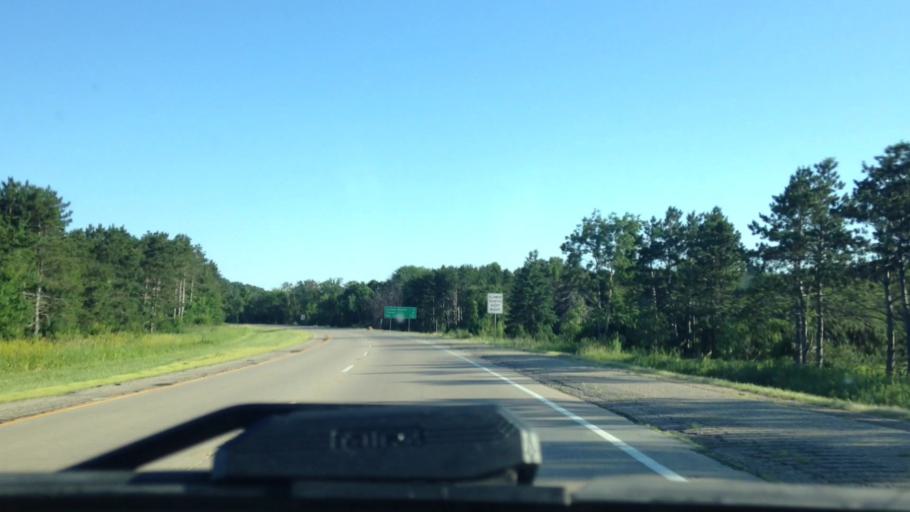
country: US
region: Wisconsin
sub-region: Columbia County
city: Wisconsin Dells
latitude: 43.6609
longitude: -89.8119
